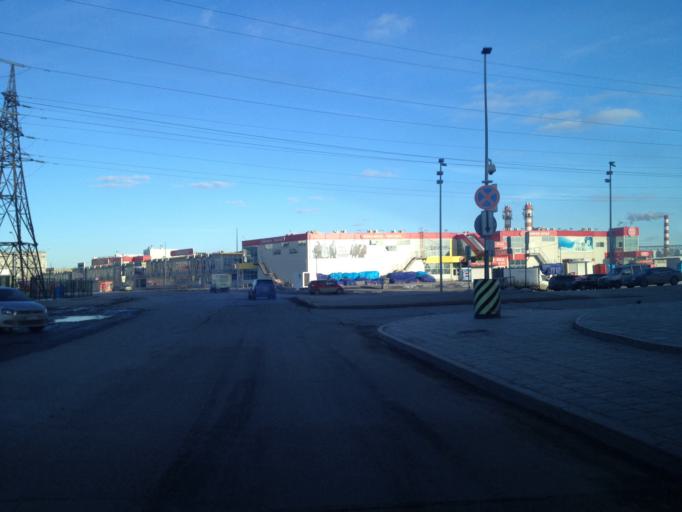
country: RU
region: Sverdlovsk
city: Yekaterinburg
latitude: 56.8618
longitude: 60.5375
